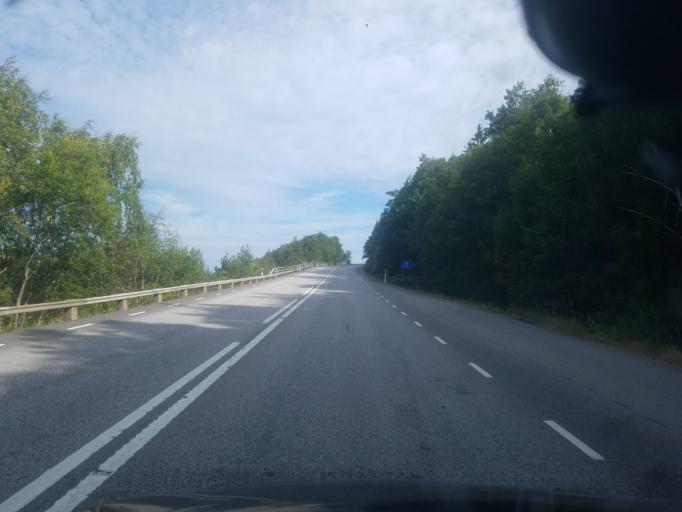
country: SE
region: Vaestra Goetaland
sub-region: Orust
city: Henan
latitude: 58.2578
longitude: 11.6781
